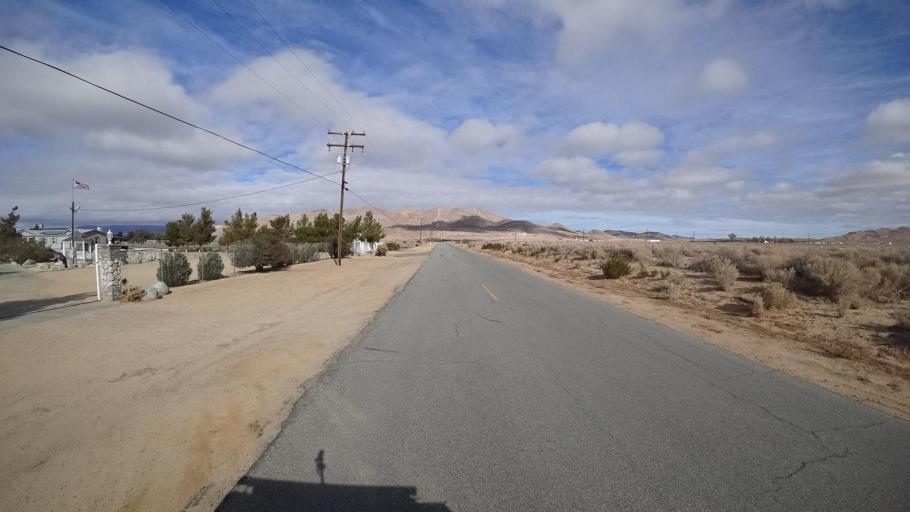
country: US
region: California
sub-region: Kern County
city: Rosamond
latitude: 34.8611
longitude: -118.2734
